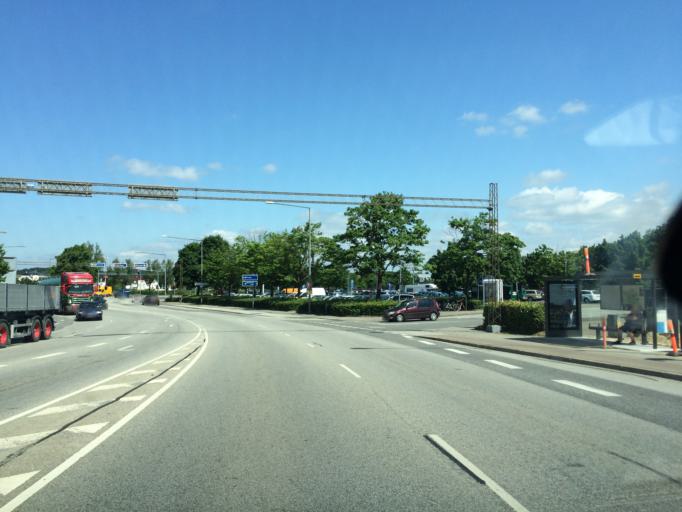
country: DK
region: Central Jutland
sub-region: Silkeborg Kommune
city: Silkeborg
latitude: 56.1708
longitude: 9.5530
